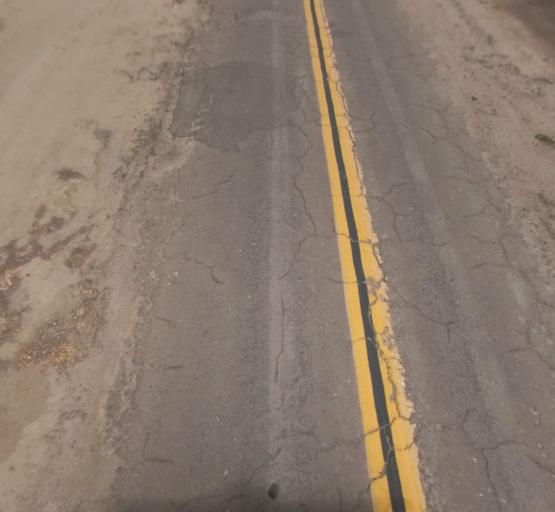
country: US
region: California
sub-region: Madera County
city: Fairmead
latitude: 36.9824
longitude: -120.2385
